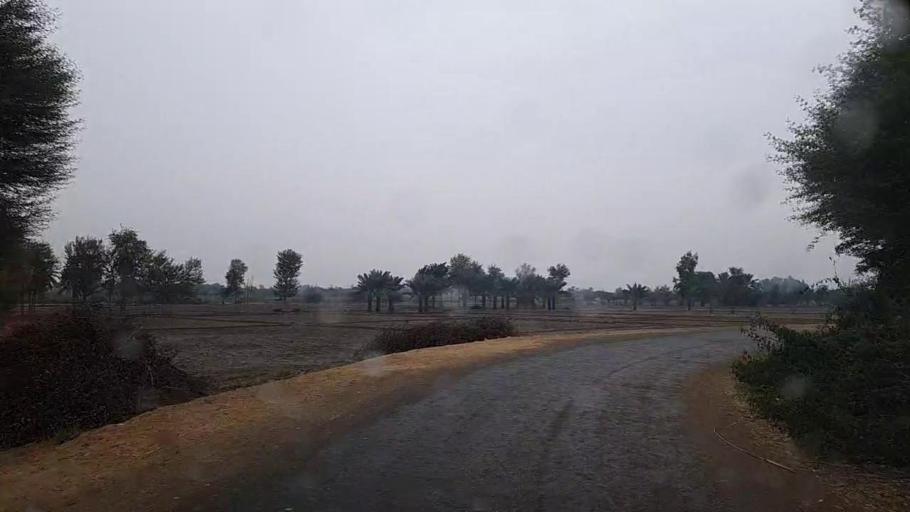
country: PK
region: Sindh
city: Ranipur
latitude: 27.2609
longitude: 68.5754
